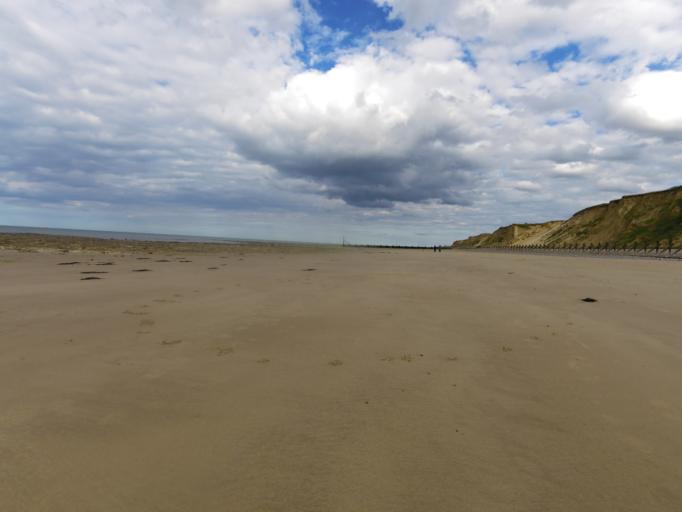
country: GB
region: England
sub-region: Norfolk
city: Sheringham
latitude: 52.9425
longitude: 1.2446
